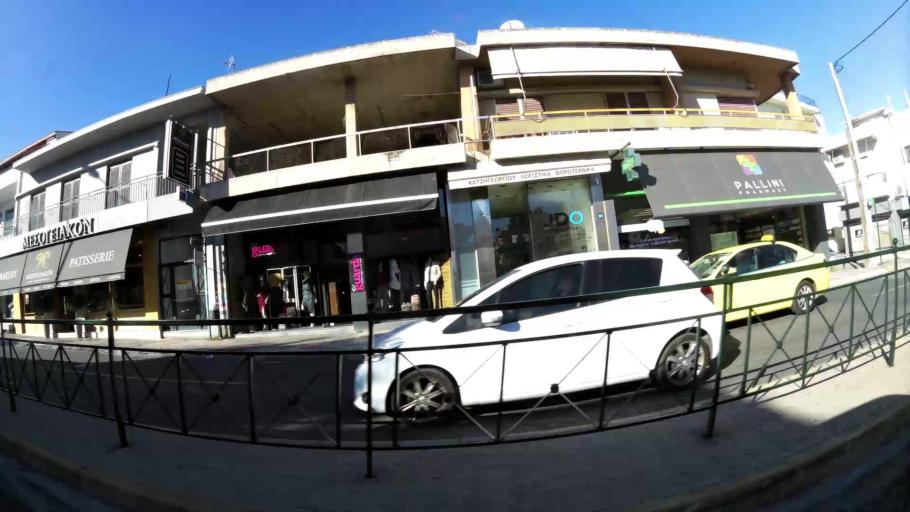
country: GR
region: Attica
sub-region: Nomarchia Anatolikis Attikis
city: Pallini
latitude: 38.0038
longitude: 23.8823
